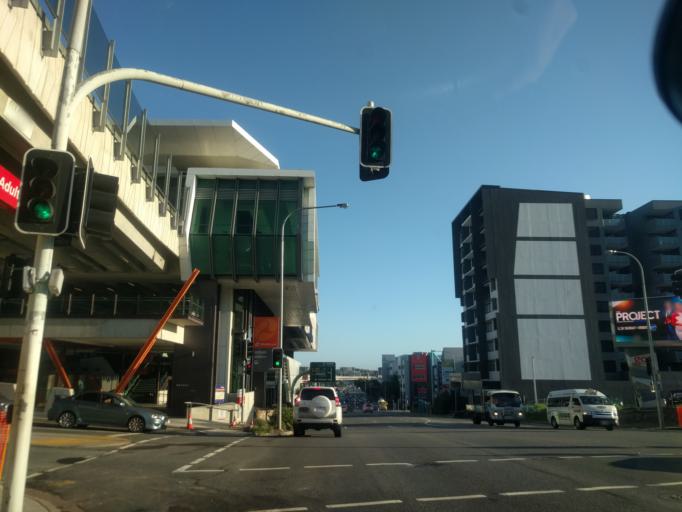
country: AU
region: Queensland
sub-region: Brisbane
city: Fortitude Valley
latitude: -27.4481
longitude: 153.0292
